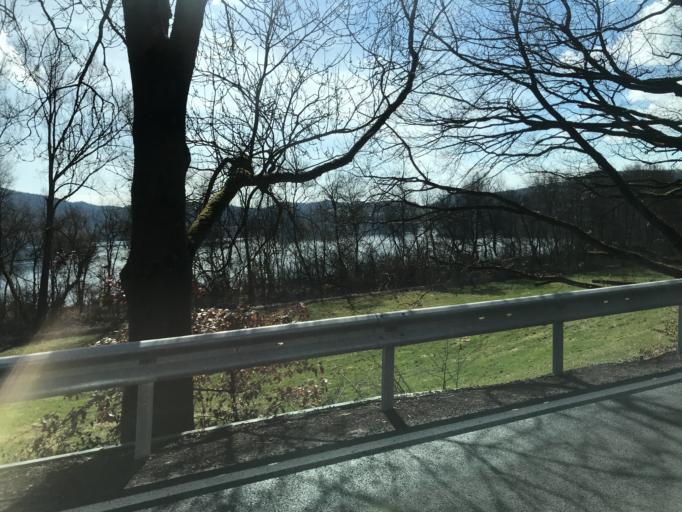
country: DE
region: Rheinland-Pfalz
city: Glees
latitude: 50.4125
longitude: 7.2555
